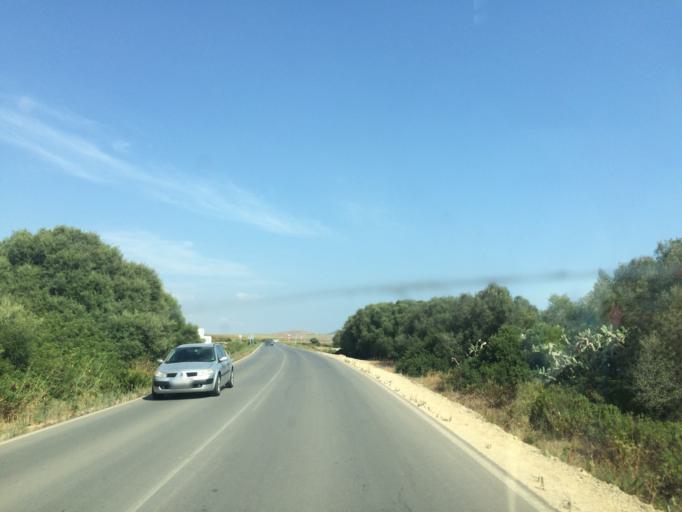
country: ES
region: Andalusia
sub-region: Provincia de Cadiz
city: Conil de la Frontera
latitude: 36.2358
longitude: -6.0514
